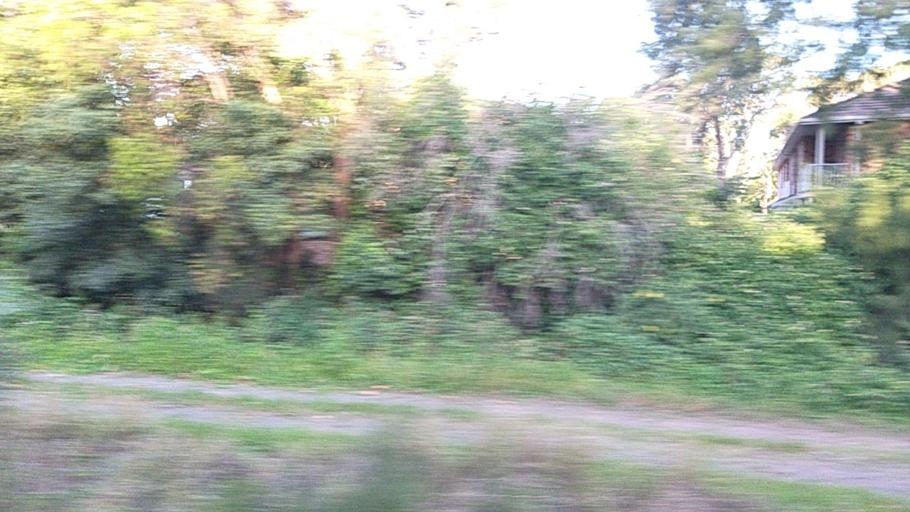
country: AU
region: New South Wales
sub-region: Hurstville
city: Oatley
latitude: -33.9782
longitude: 151.0785
